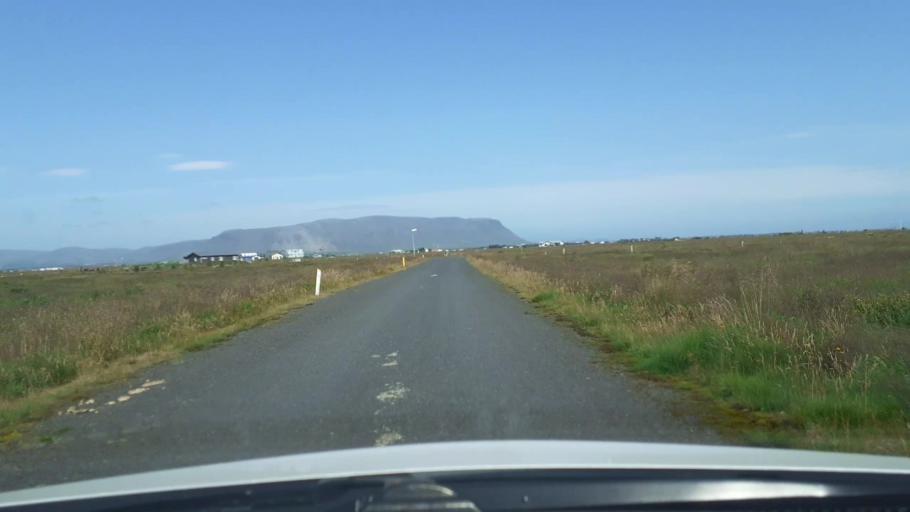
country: IS
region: South
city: Selfoss
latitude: 63.8895
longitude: -21.0860
